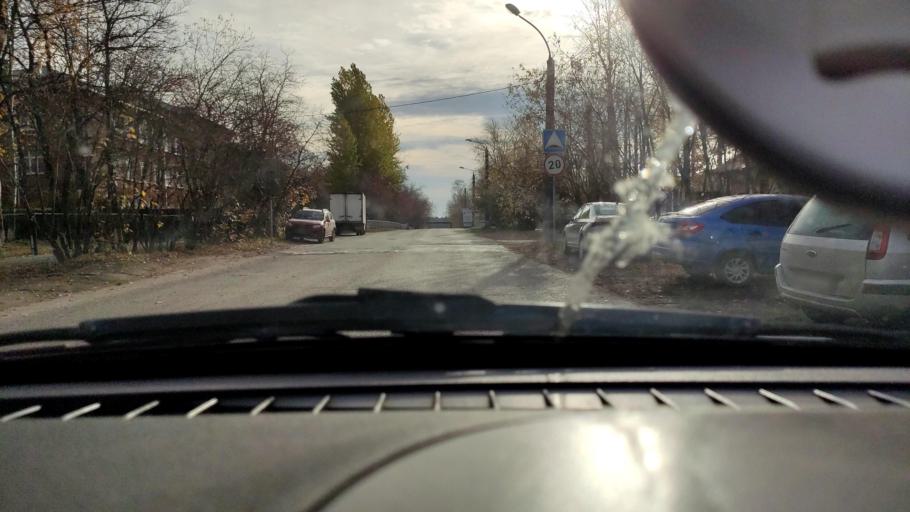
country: RU
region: Perm
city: Perm
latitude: 58.0862
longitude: 56.3923
